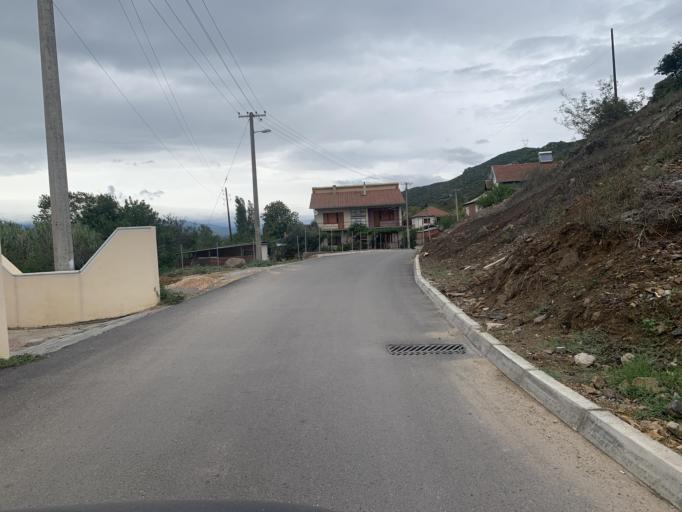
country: MK
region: Bogdanci
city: Bogdanci
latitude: 41.1903
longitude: 22.5398
